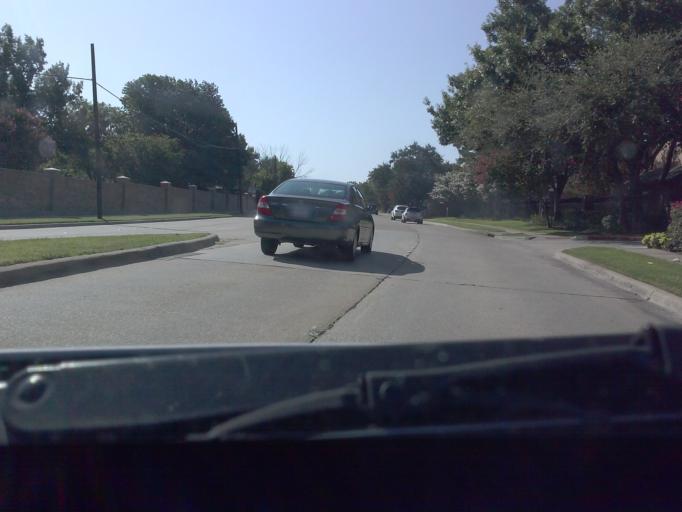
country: US
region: Texas
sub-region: Dallas County
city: Addison
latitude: 33.0302
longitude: -96.7895
